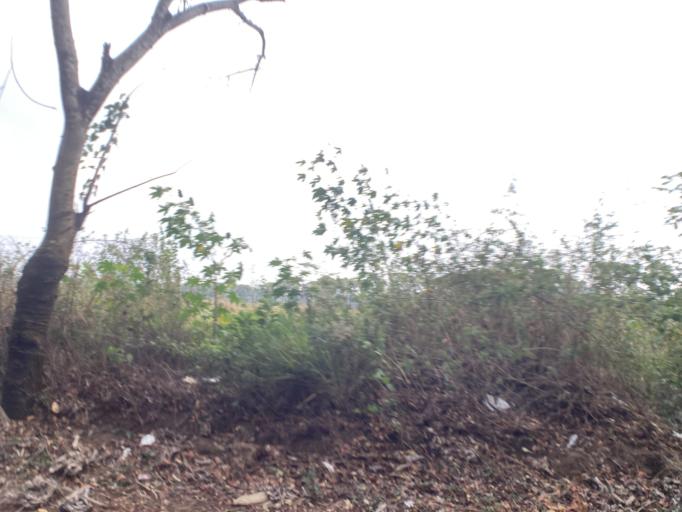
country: GT
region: Guatemala
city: Fraijanes
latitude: 14.3912
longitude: -90.4854
